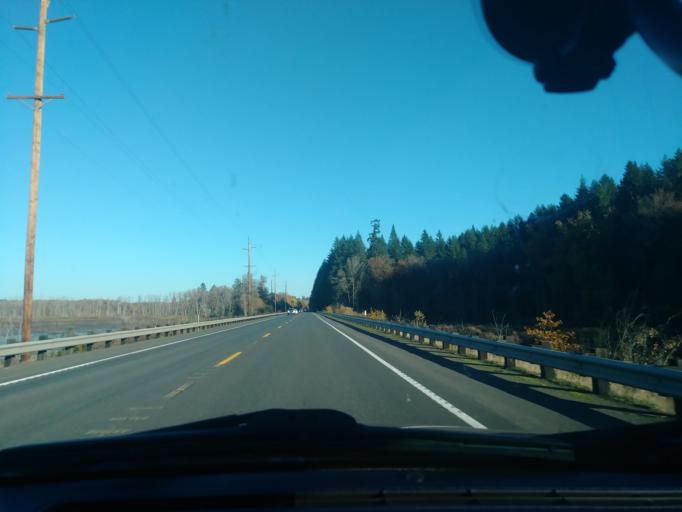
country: US
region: Oregon
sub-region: Washington County
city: Banks
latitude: 45.6110
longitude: -123.1456
